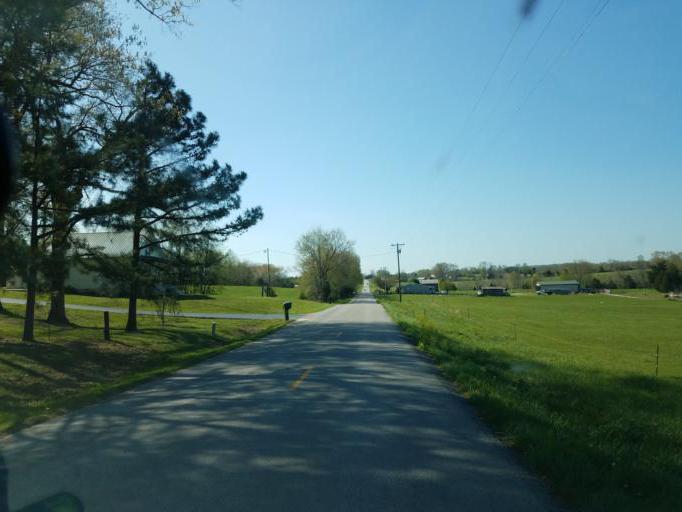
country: US
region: Kentucky
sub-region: Edmonson County
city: Brownsville
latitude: 37.1256
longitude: -86.1583
